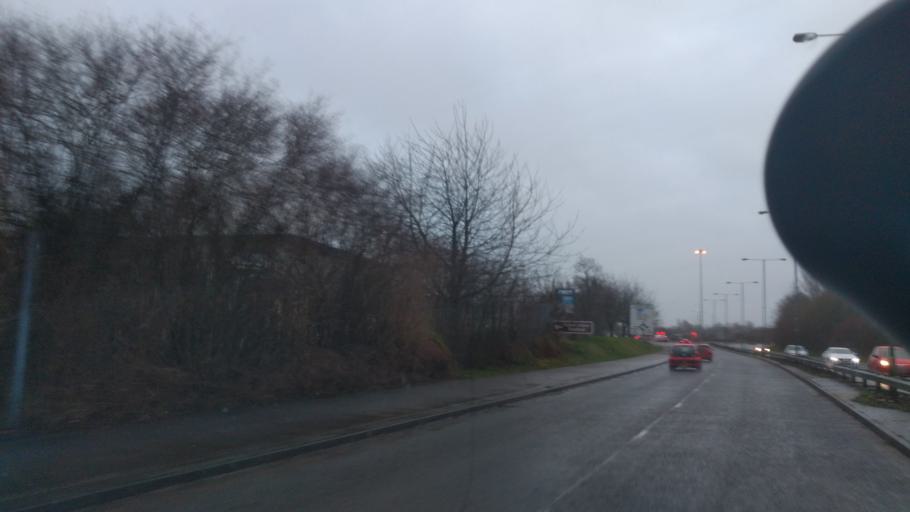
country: GB
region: England
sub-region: Borough of Swindon
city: Swindon
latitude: 51.5792
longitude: -1.7753
